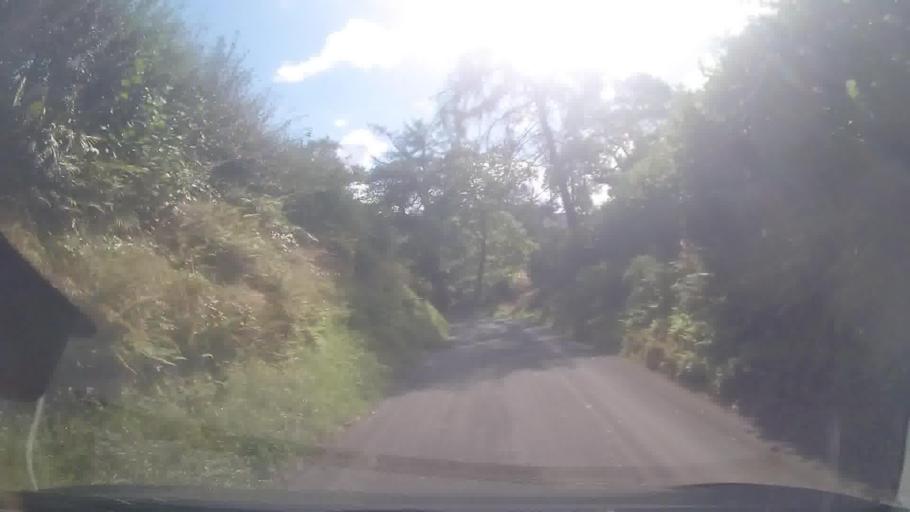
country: GB
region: Wales
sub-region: Gwynedd
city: Bala
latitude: 52.7748
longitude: -3.6242
